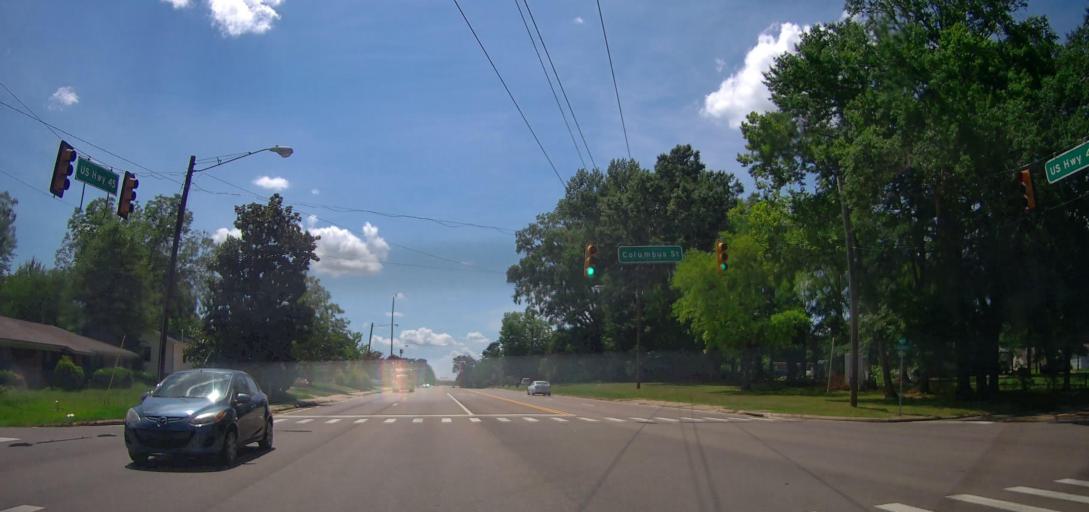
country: US
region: Mississippi
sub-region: Monroe County
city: Aberdeen
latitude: 33.8151
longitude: -88.5474
